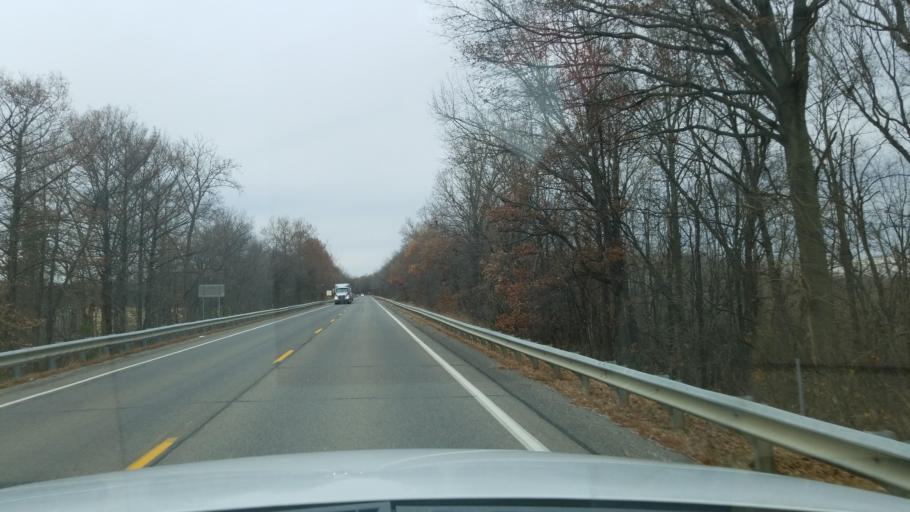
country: US
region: Indiana
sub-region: Posey County
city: Mount Vernon
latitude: 37.9394
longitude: -88.0131
